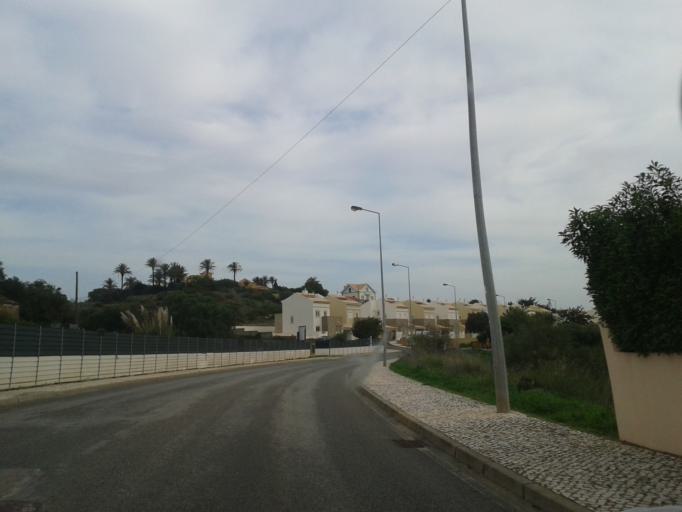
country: PT
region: Faro
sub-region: Lagos
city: Lagos
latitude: 37.0910
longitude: -8.7359
